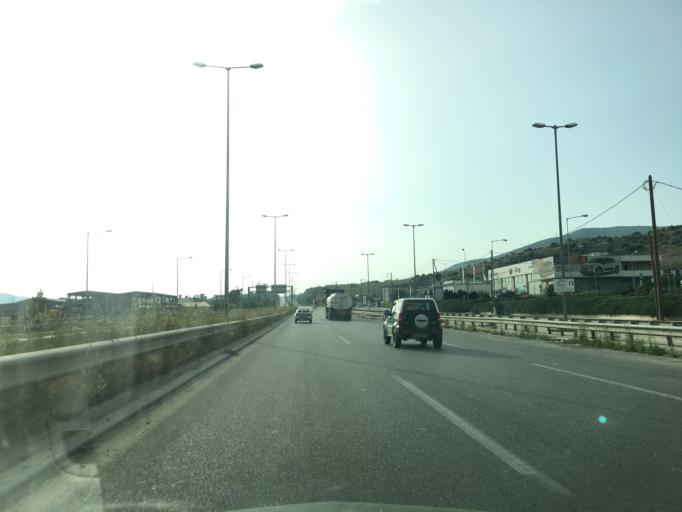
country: GR
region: Thessaly
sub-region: Nomos Magnisias
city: Nea Ionia
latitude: 39.3749
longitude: 22.8997
